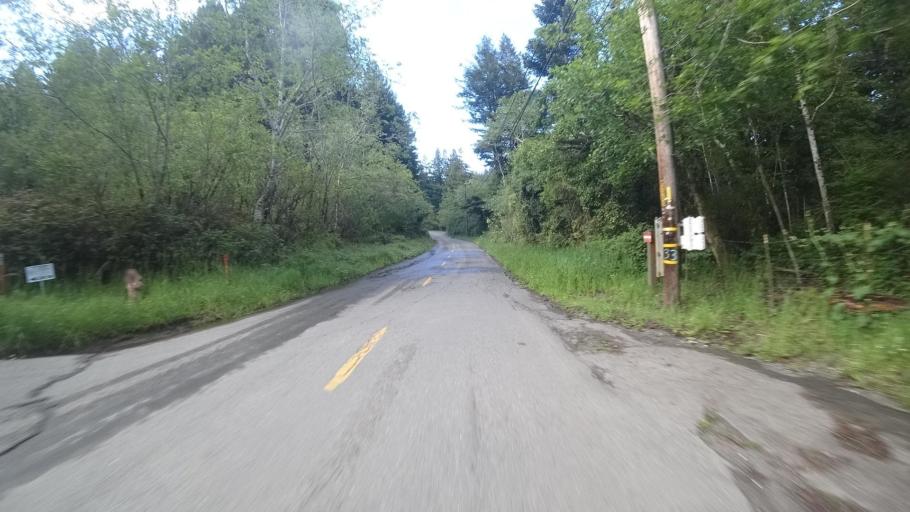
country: US
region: California
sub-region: Humboldt County
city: Westhaven-Moonstone
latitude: 41.0501
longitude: -124.1196
